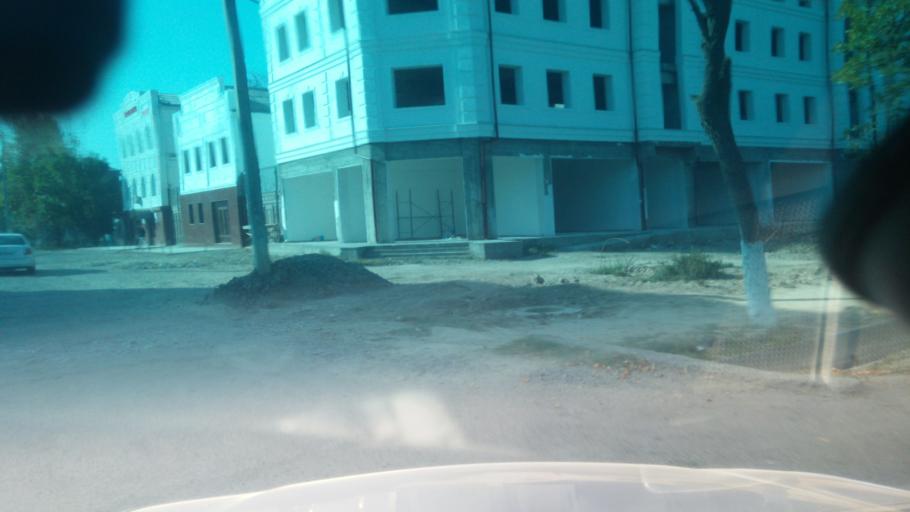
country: UZ
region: Sirdaryo
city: Guliston
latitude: 40.4980
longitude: 68.7687
